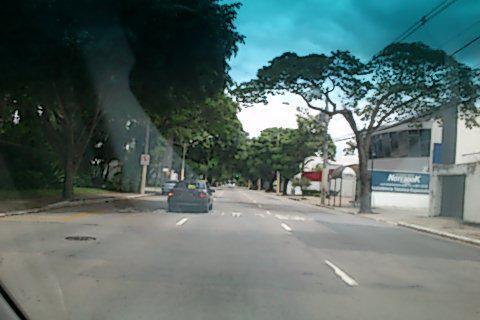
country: BR
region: Sao Paulo
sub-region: Sao Jose Dos Campos
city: Sao Jose dos Campos
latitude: -23.1975
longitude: -45.8991
